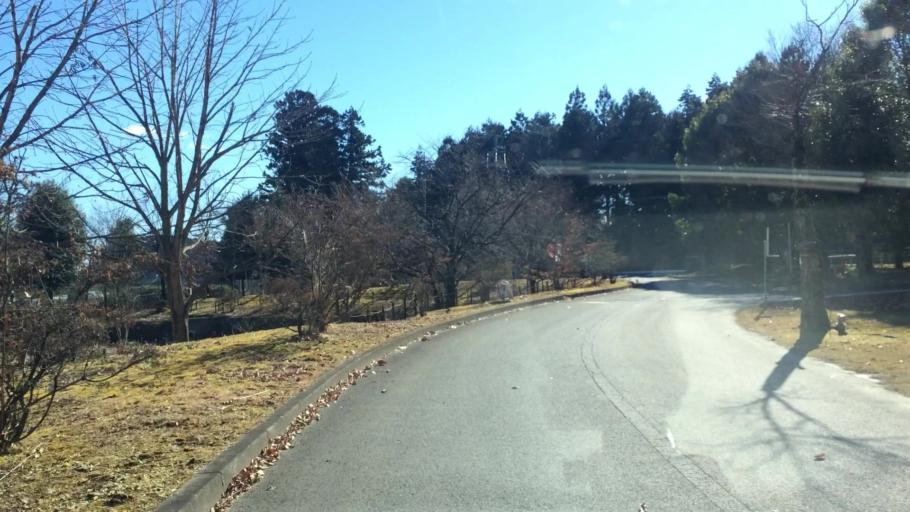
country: JP
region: Tochigi
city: Imaichi
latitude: 36.7459
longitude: 139.7462
